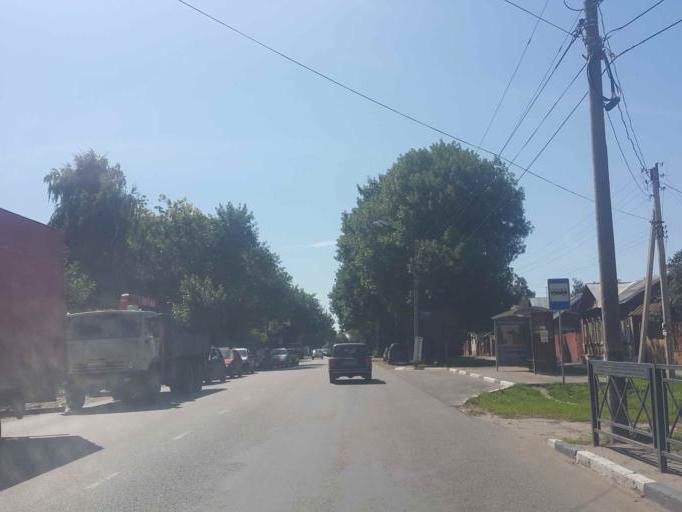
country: RU
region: Tambov
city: Tambov
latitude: 52.7188
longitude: 41.4238
